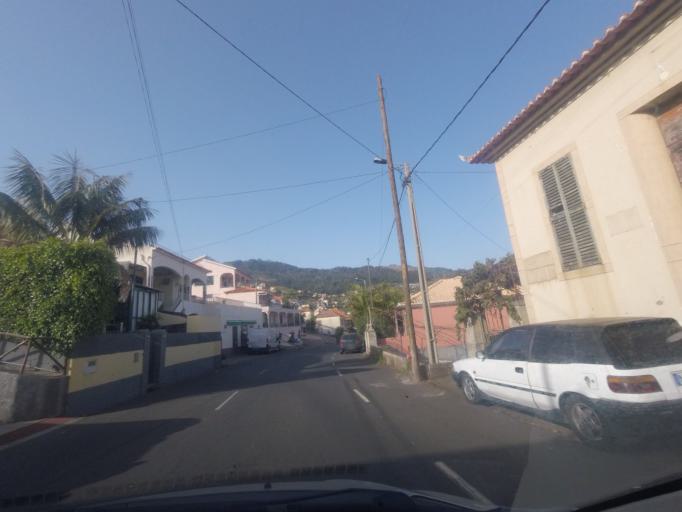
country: PT
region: Madeira
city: Ponta do Sol
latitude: 32.6980
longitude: -17.1156
